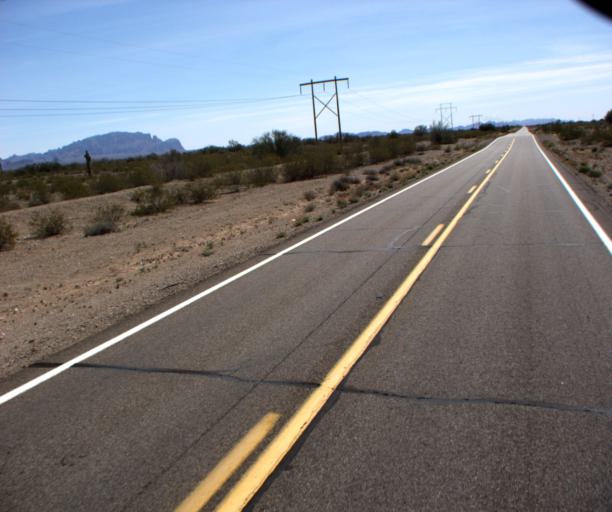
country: US
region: Arizona
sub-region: La Paz County
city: Quartzsite
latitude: 33.5107
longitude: -114.2170
